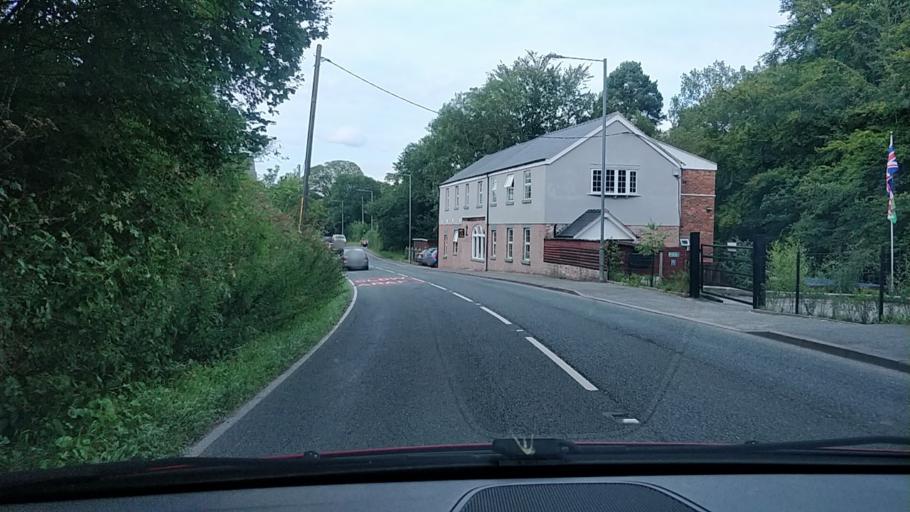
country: GB
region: Wales
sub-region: County of Flintshire
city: Leeswood
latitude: 53.1334
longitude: -3.0816
